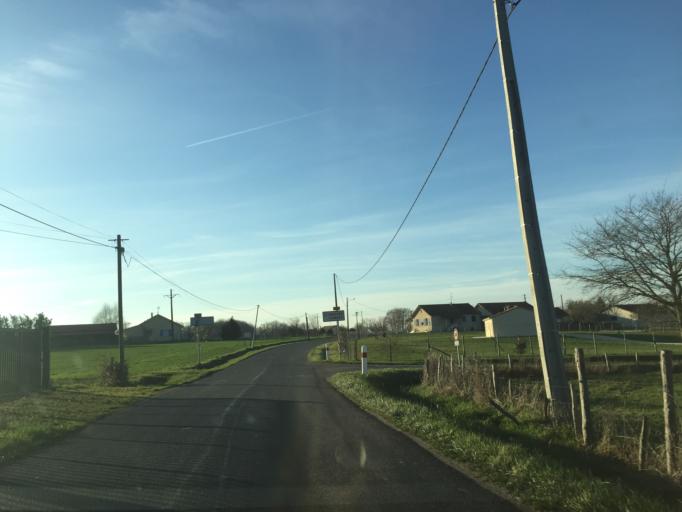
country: FR
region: Aquitaine
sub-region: Departement de la Dordogne
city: Saint-Aulaye
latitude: 45.2532
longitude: 0.2044
